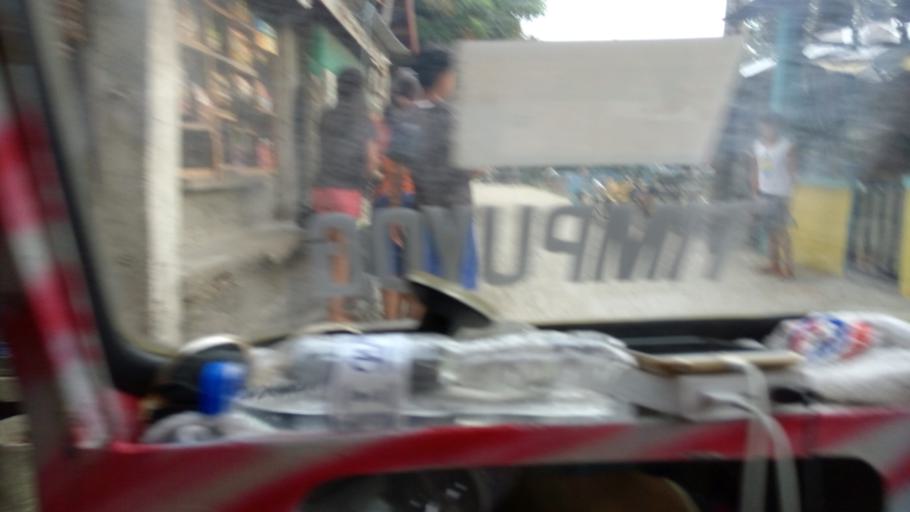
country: PH
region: Ilocos
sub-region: Province of La Union
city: Damortis
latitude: 16.2495
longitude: 120.4029
